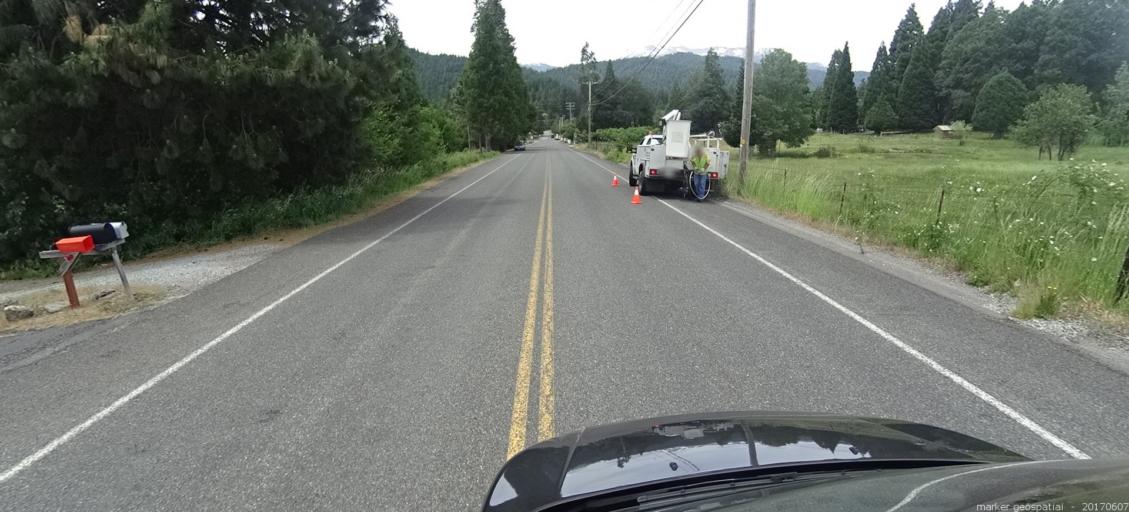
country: US
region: California
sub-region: Siskiyou County
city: Mount Shasta
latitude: 41.2980
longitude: -122.3190
